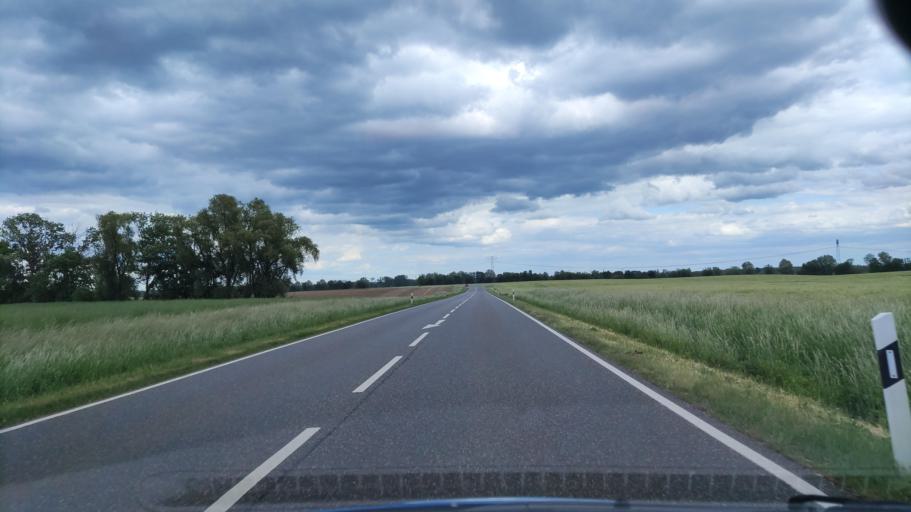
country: DE
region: Mecklenburg-Vorpommern
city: Neuburg
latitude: 53.4432
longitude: 11.9058
